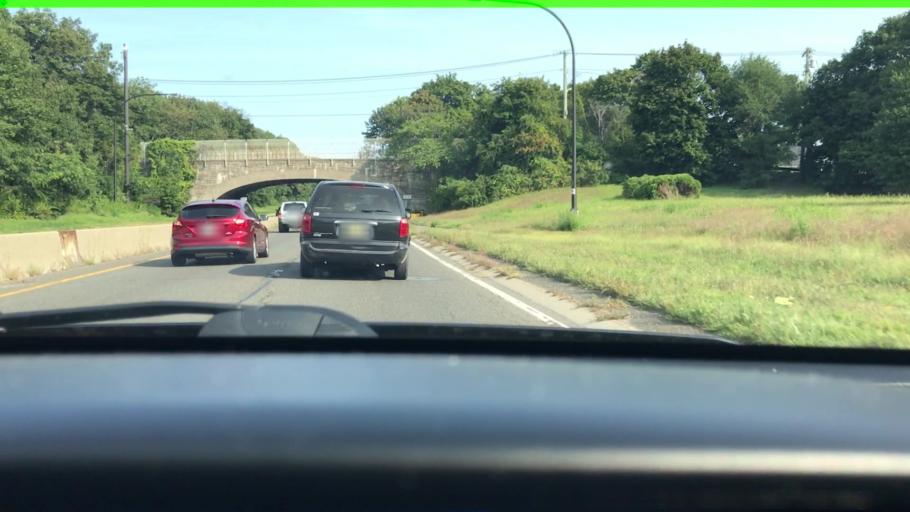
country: US
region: New York
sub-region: Nassau County
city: Salisbury
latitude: 40.7475
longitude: -73.5472
